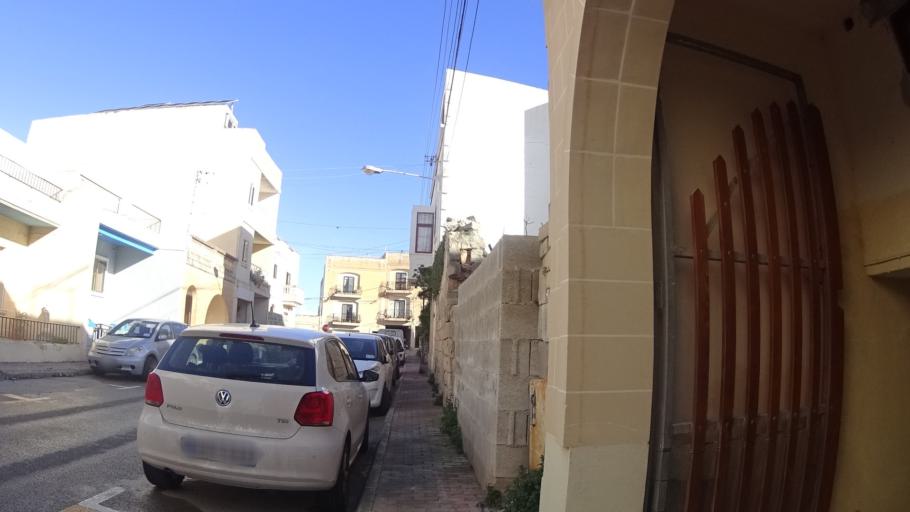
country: MT
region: Hal Gharghur
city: Hal Gharghur
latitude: 35.9247
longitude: 14.4516
